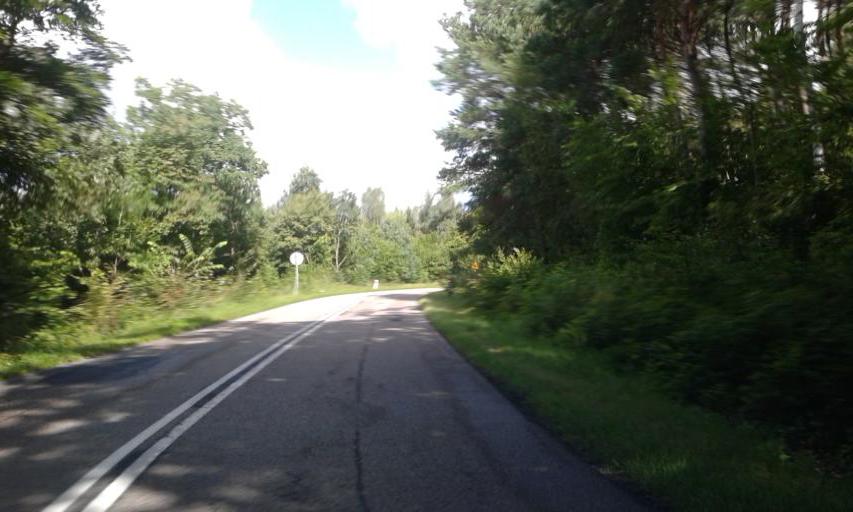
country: PL
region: West Pomeranian Voivodeship
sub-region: Powiat koszalinski
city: Polanow
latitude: 54.0026
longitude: 16.7154
